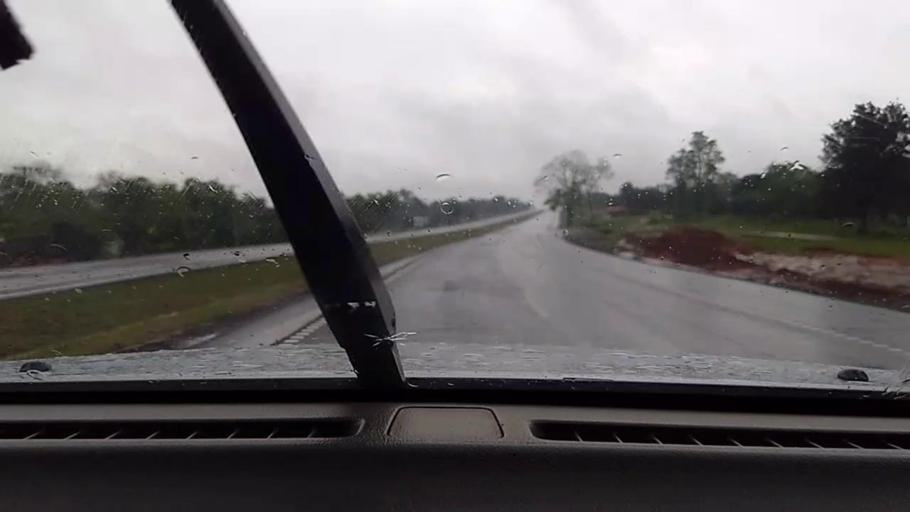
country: PY
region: Caaguazu
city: Repatriacion
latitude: -25.4664
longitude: -55.9358
